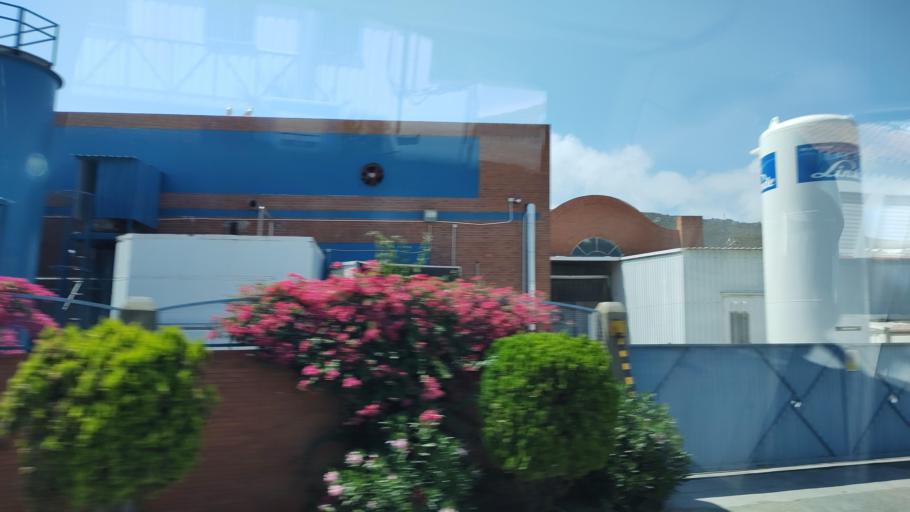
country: ES
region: Andalusia
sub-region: Provincia de Cadiz
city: La Linea de la Concepcion
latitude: 36.1875
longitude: -5.3492
